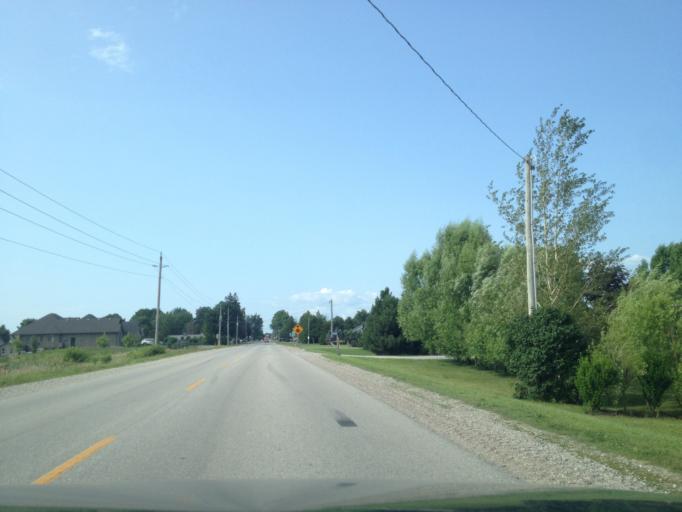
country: CA
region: Ontario
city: Aylmer
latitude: 42.7076
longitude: -80.8591
